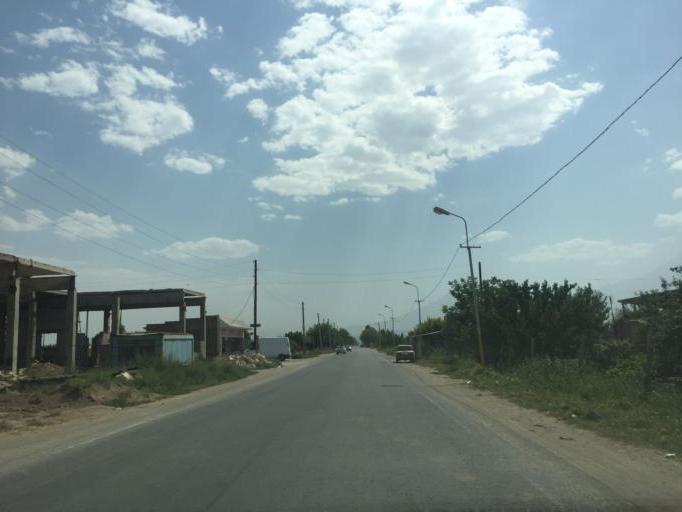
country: AM
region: Ararat
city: Shahumyan
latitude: 39.8965
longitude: 44.5971
